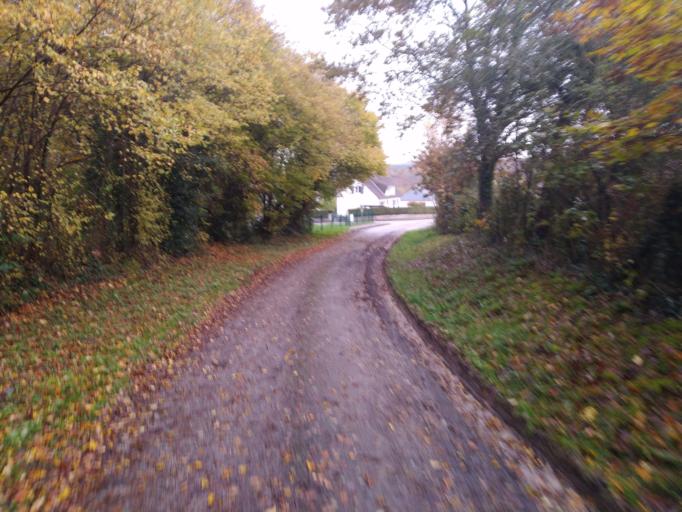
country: FR
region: Haute-Normandie
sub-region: Departement de la Seine-Maritime
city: Yainville
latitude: 49.4537
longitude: 0.8371
